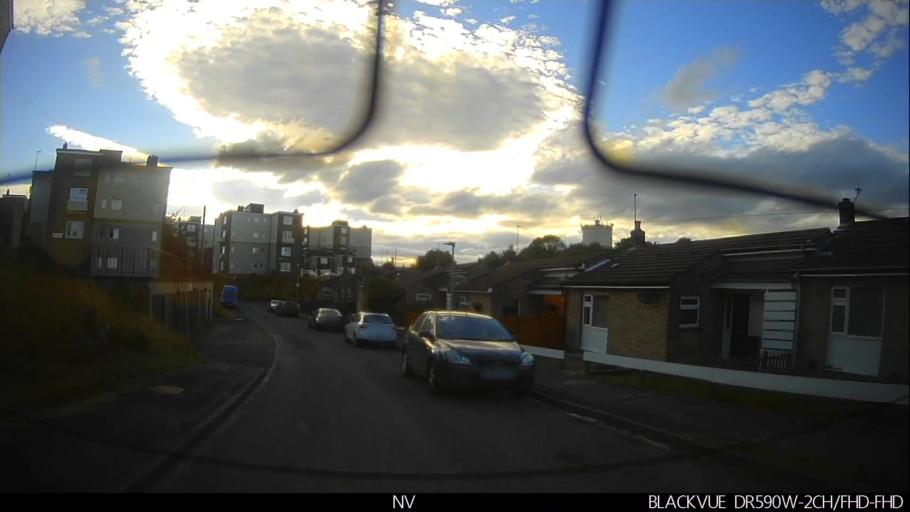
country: GB
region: England
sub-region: City of York
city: York
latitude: 53.9575
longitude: -1.1159
